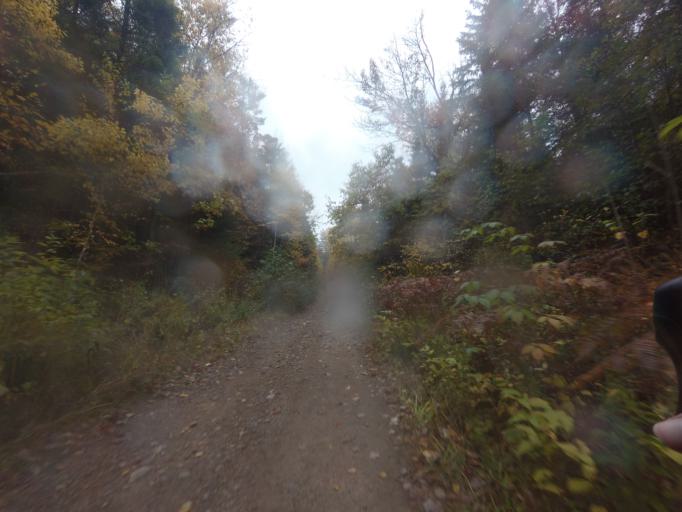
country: CA
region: Ontario
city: Petawawa
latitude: 45.7861
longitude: -77.3810
